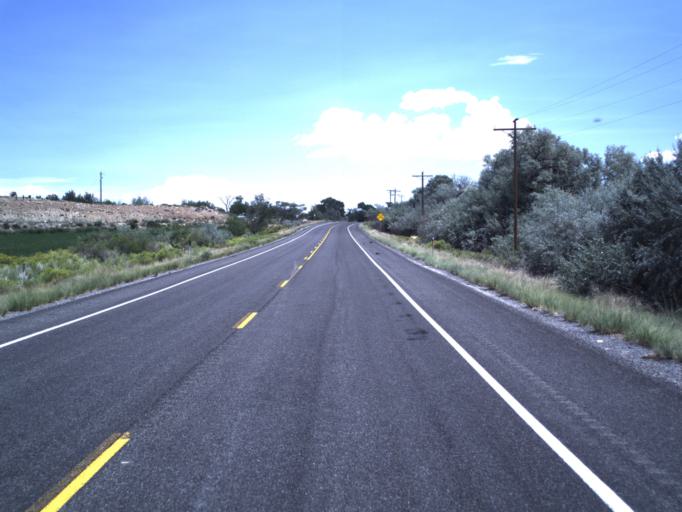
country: US
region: Utah
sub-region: Emery County
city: Huntington
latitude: 39.3521
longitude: -111.0068
